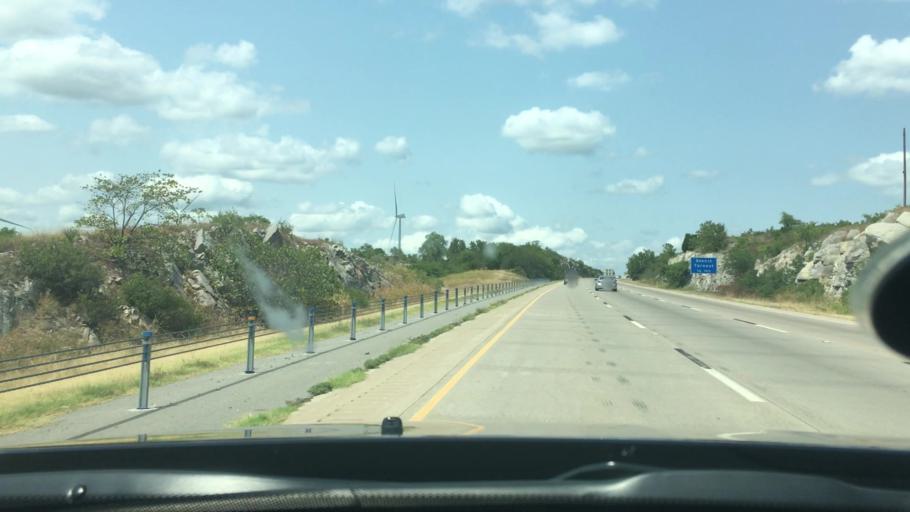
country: US
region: Oklahoma
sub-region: Murray County
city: Davis
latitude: 34.3692
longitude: -97.1459
